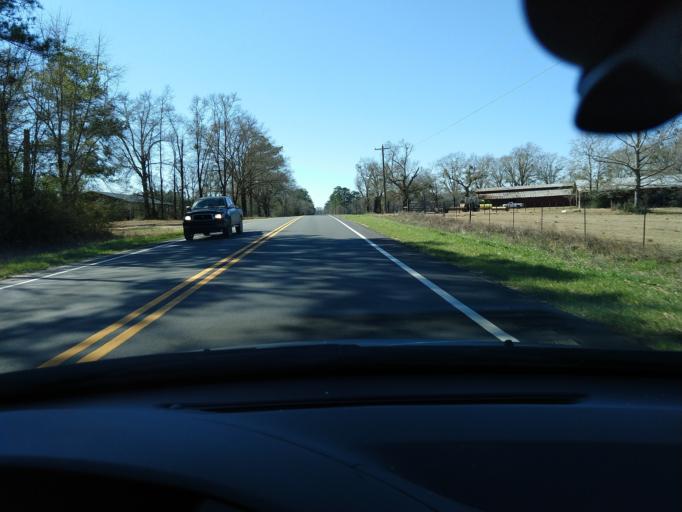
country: US
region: Alabama
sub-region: Covington County
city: Andalusia
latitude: 31.1948
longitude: -86.5633
